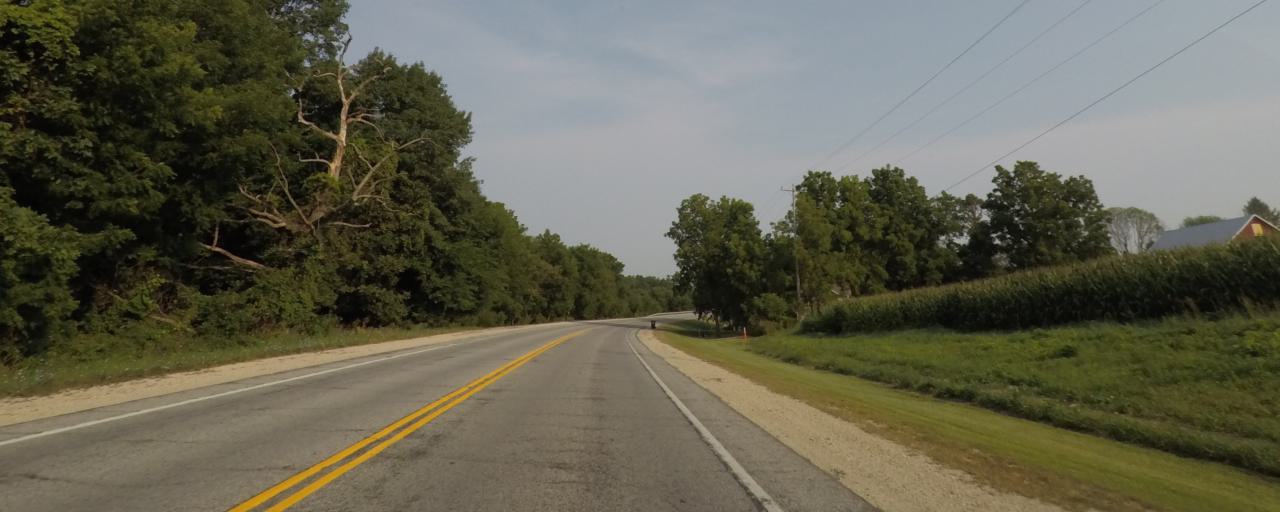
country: US
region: Wisconsin
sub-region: Dane County
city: Deerfield
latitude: 43.0874
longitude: -89.0783
